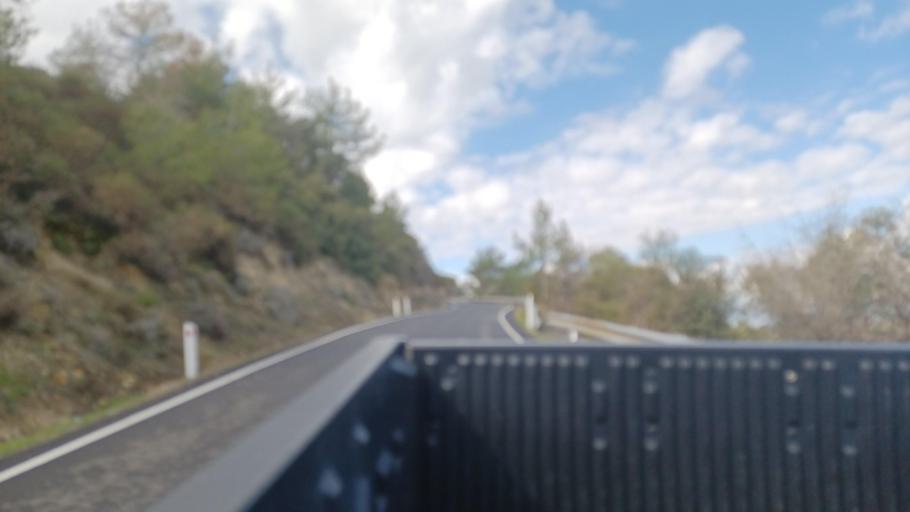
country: CY
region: Limassol
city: Pissouri
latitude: 34.7462
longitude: 32.6628
